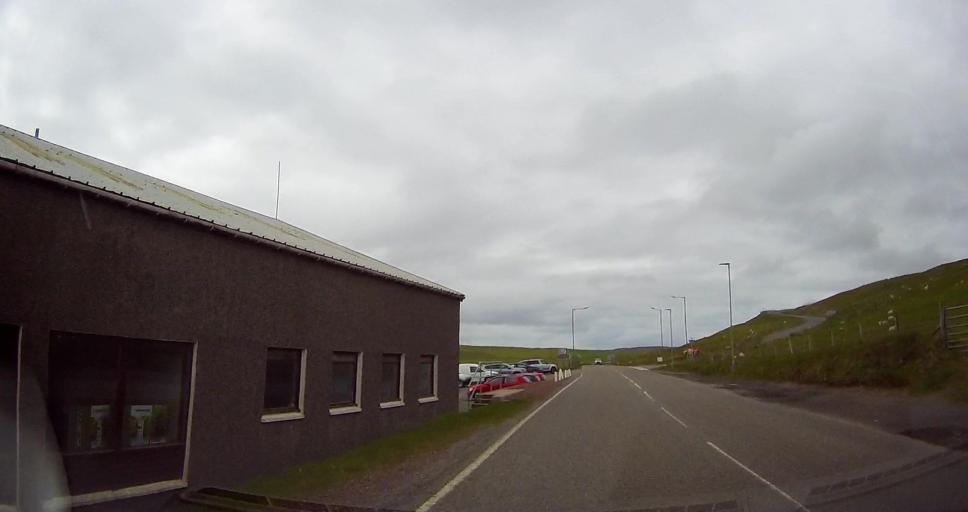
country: GB
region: Scotland
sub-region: Shetland Islands
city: Lerwick
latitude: 60.2533
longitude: -1.4032
